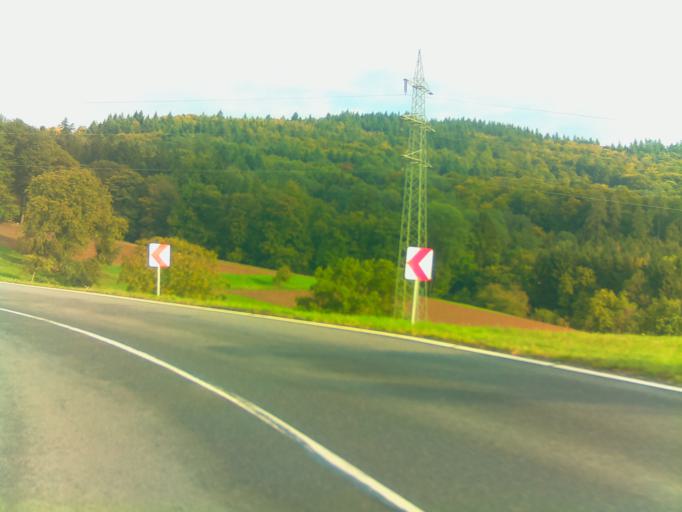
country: DE
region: Hesse
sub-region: Regierungsbezirk Darmstadt
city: Lindenfels
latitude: 49.6807
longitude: 8.8050
